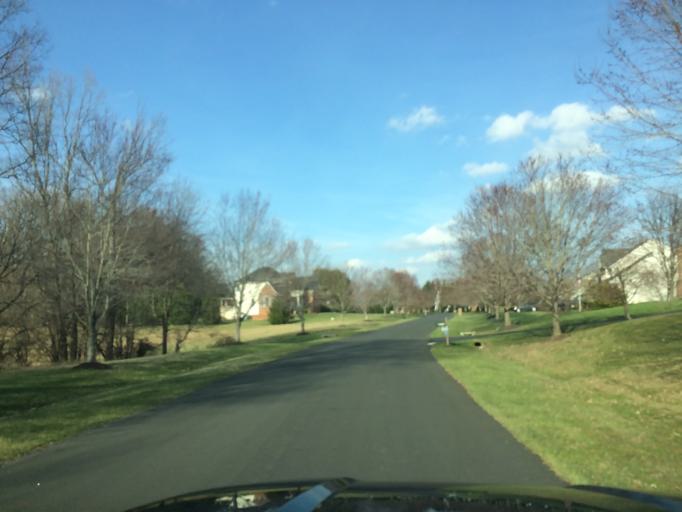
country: US
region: Maryland
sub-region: Carroll County
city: Sykesville
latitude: 39.2838
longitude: -76.9776
